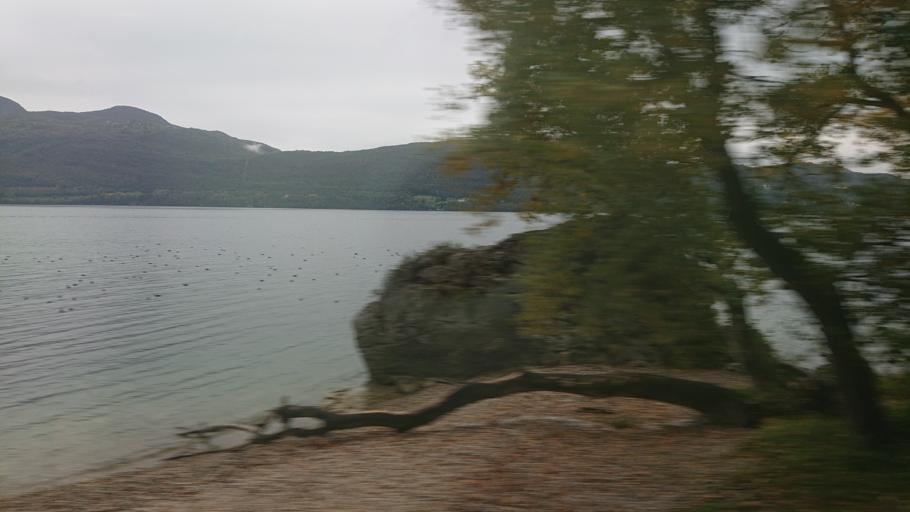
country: FR
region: Rhone-Alpes
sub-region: Departement de la Savoie
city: Chatillon
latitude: 45.7813
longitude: 5.8640
